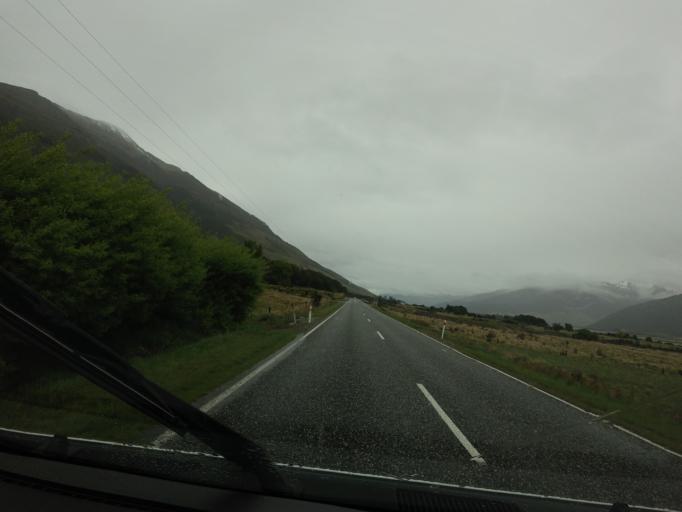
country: NZ
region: Otago
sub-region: Queenstown-Lakes District
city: Wanaka
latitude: -44.2345
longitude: 169.2302
